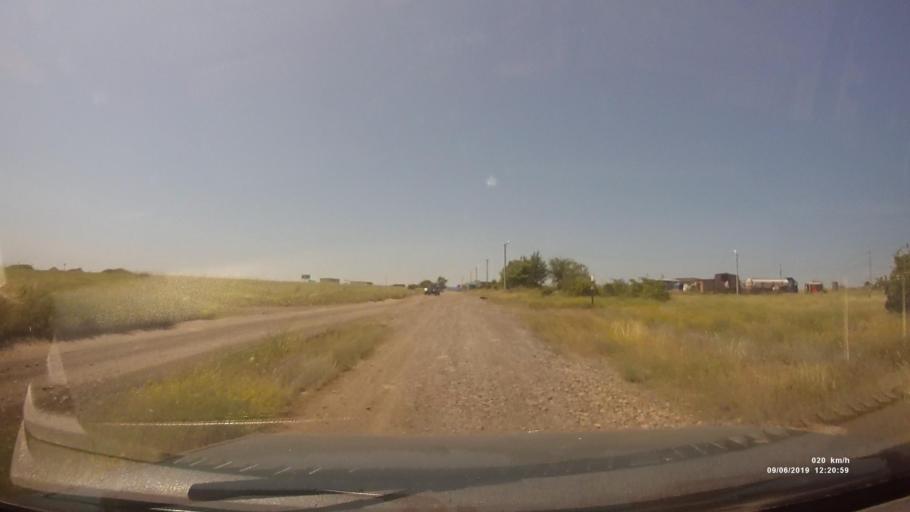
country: RU
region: Rostov
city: Kamensk-Shakhtinskiy
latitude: 48.2511
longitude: 40.2978
